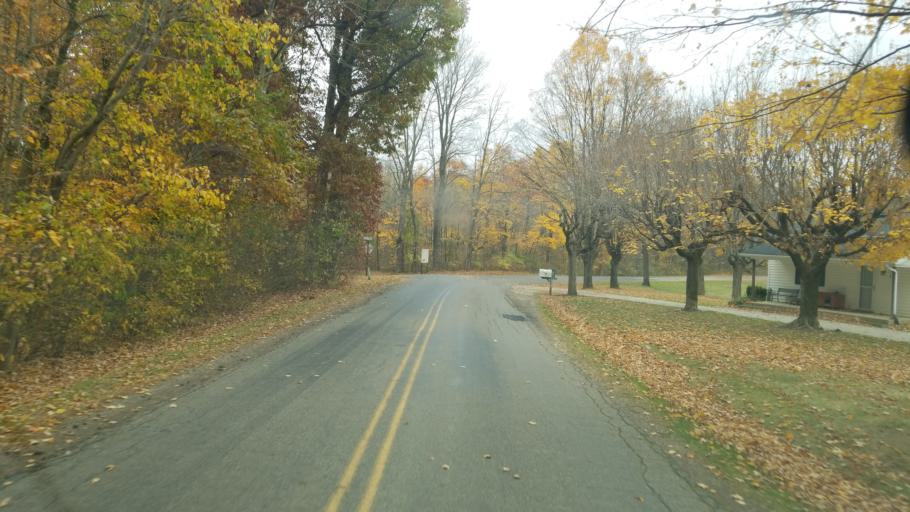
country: US
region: Ohio
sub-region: Licking County
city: Utica
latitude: 40.2770
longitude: -82.4262
